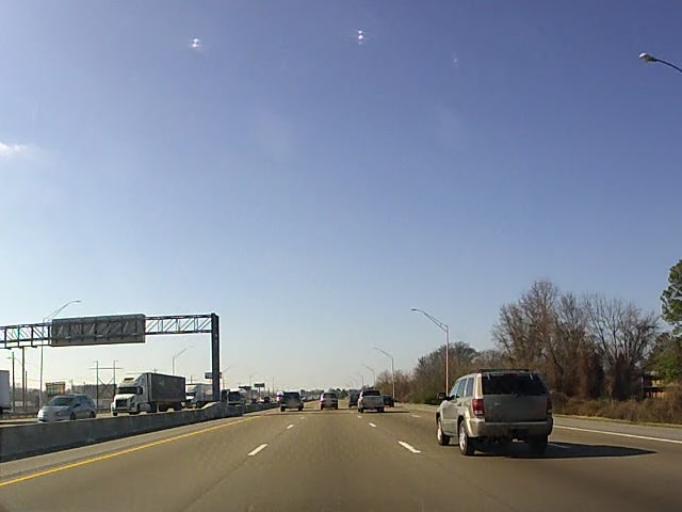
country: US
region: Tennessee
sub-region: Shelby County
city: New South Memphis
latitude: 35.0770
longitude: -89.9720
